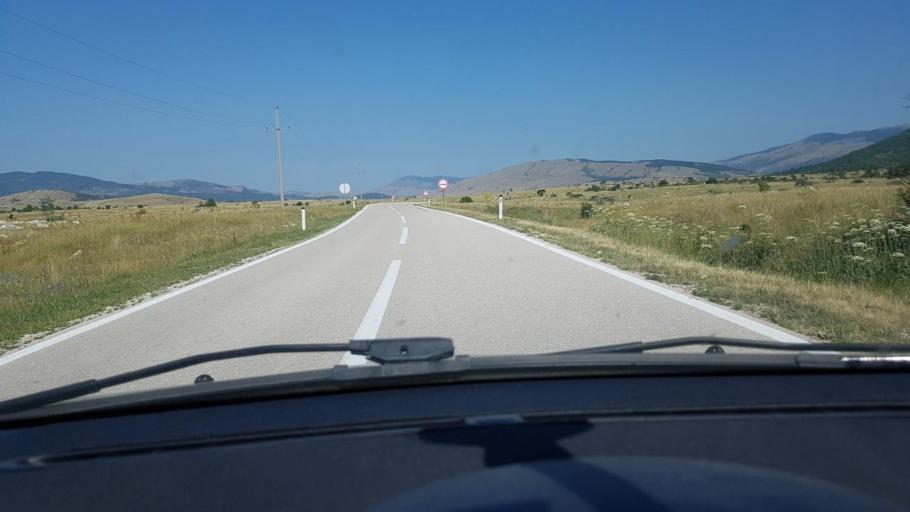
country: BA
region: Federation of Bosnia and Herzegovina
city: Bosansko Grahovo
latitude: 44.1426
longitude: 16.4659
